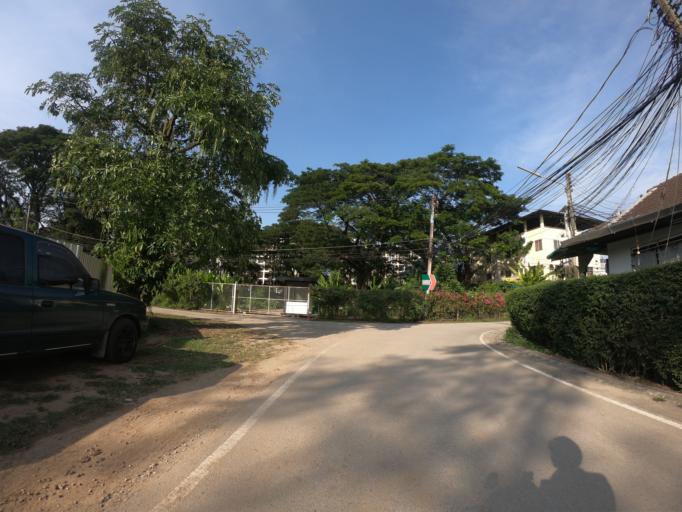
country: TH
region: Chiang Mai
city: Chiang Mai
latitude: 18.8205
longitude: 99.0136
